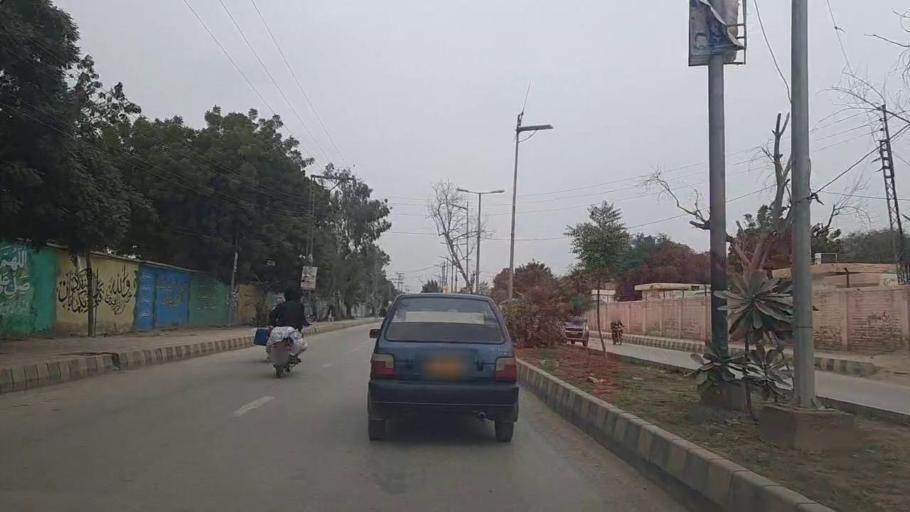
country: PK
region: Sindh
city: Nawabshah
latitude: 26.2457
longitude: 68.4017
